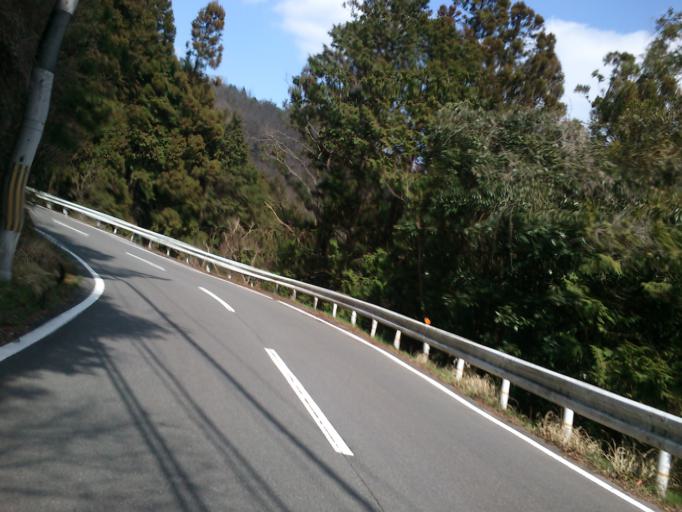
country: JP
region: Mie
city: Ueno-ebisumachi
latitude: 34.7430
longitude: 136.0039
